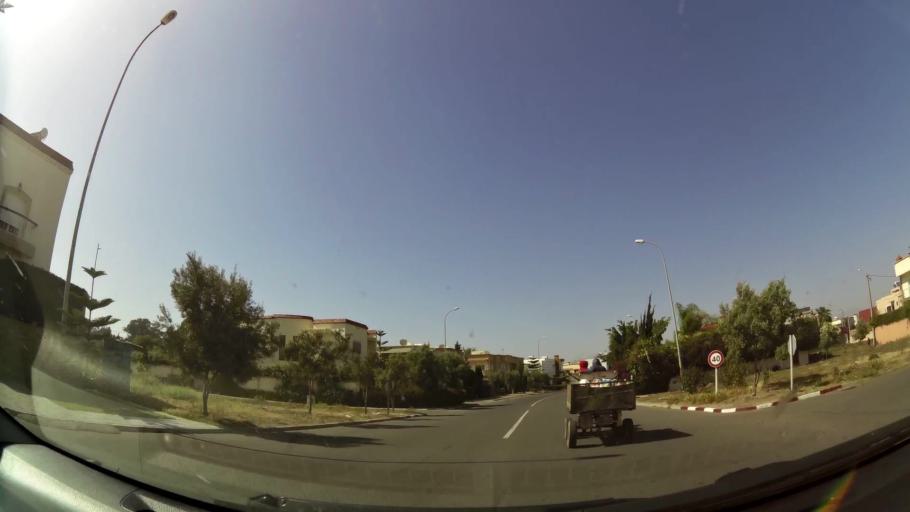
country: MA
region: Souss-Massa-Draa
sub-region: Inezgane-Ait Mellou
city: Inezgane
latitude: 30.3606
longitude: -9.5500
